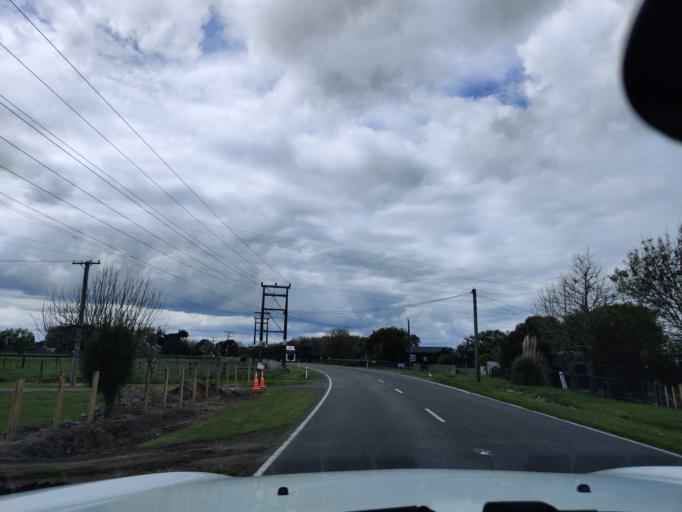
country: NZ
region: Manawatu-Wanganui
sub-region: Palmerston North City
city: Palmerston North
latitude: -40.2432
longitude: 175.5560
